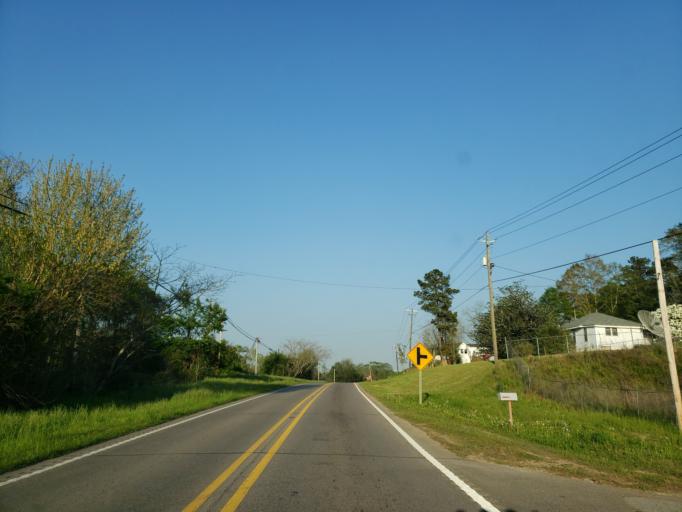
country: US
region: Mississippi
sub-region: Lauderdale County
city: Marion
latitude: 32.3937
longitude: -88.6482
